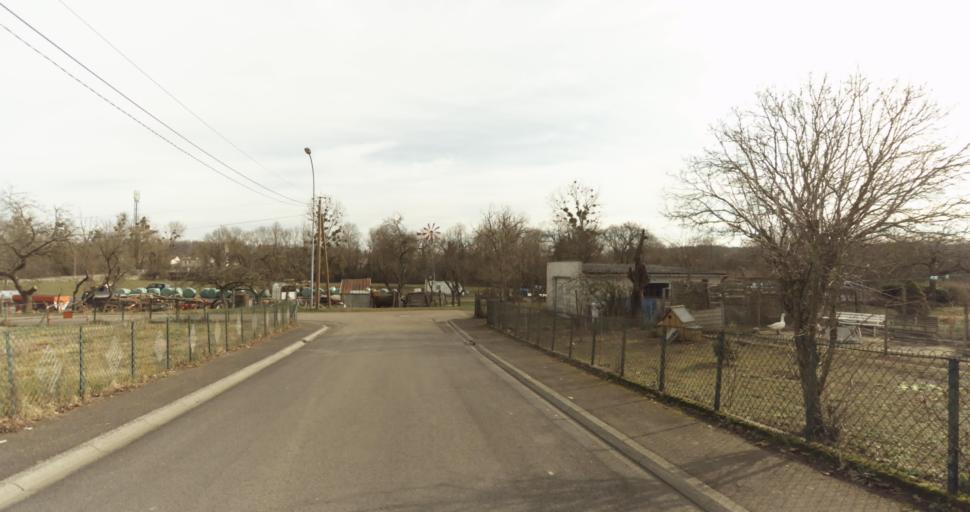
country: FR
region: Lorraine
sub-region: Departement de Meurthe-et-Moselle
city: Jarny
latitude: 49.1411
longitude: 5.8737
